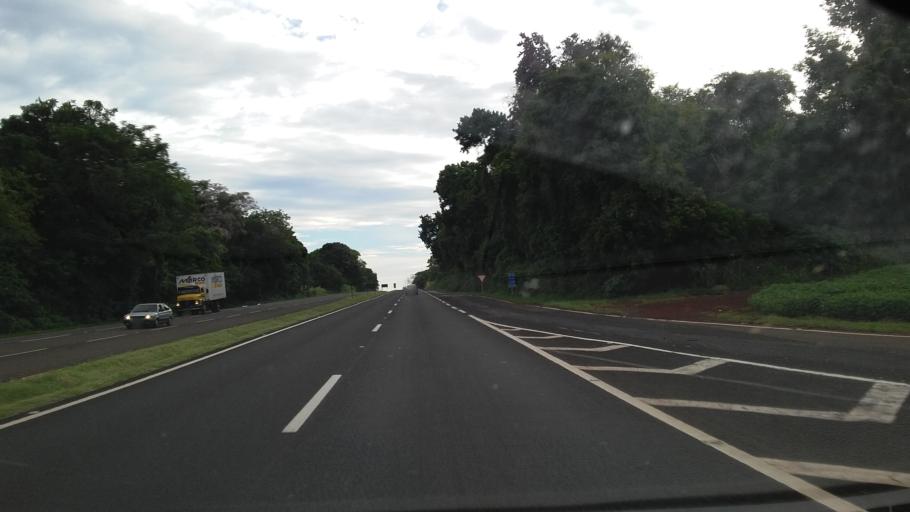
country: BR
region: Parana
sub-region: Paicandu
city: Paicandu
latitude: -23.5050
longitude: -52.0203
